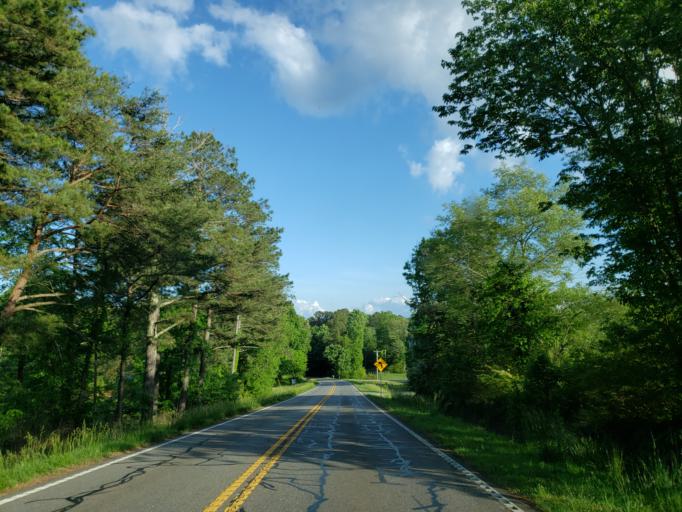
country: US
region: Georgia
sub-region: Cherokee County
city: Canton
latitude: 34.3430
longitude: -84.5777
